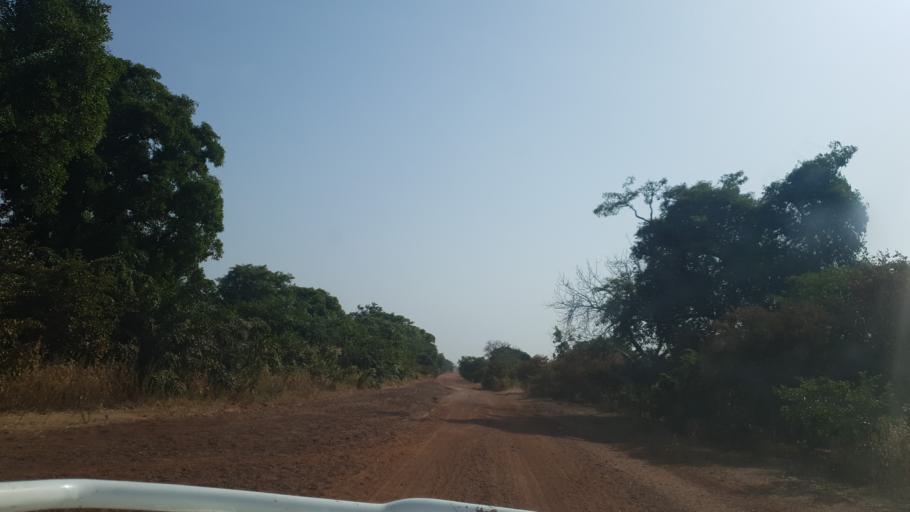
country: ML
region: Koulikoro
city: Dioila
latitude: 12.6684
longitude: -6.6836
